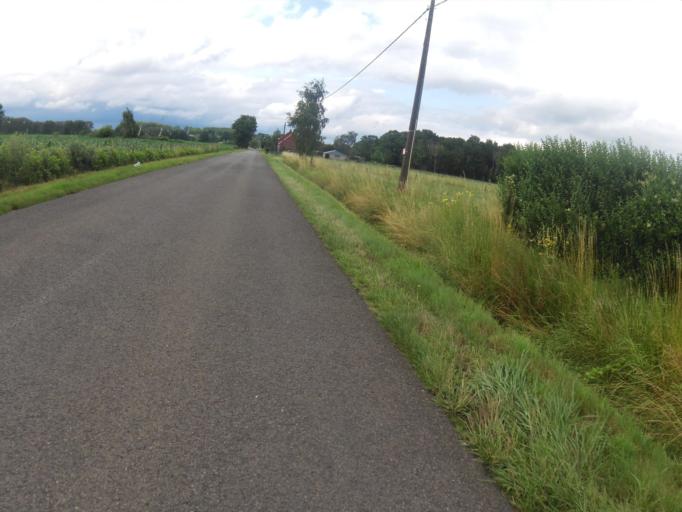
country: BE
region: Flanders
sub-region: Provincie Antwerpen
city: Geel
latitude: 51.1937
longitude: 4.9966
